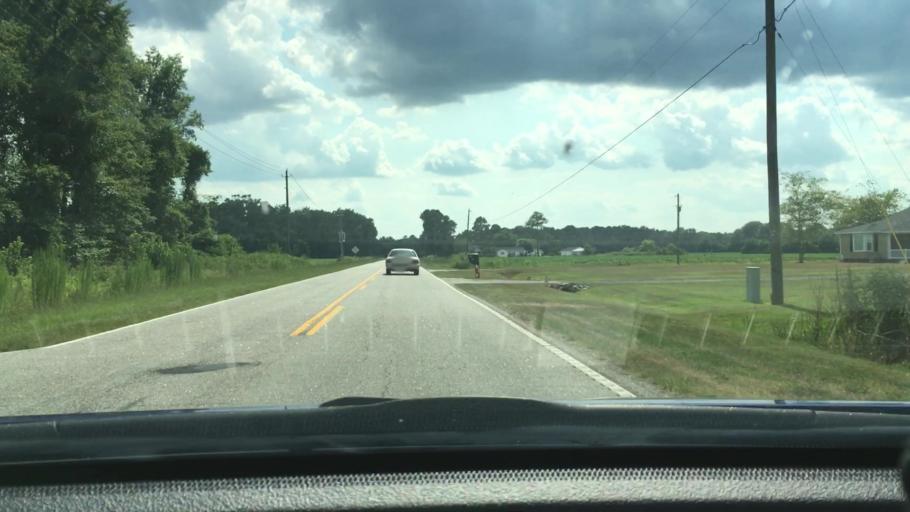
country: US
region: South Carolina
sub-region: Florence County
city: Timmonsville
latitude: 34.1614
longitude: -80.0730
